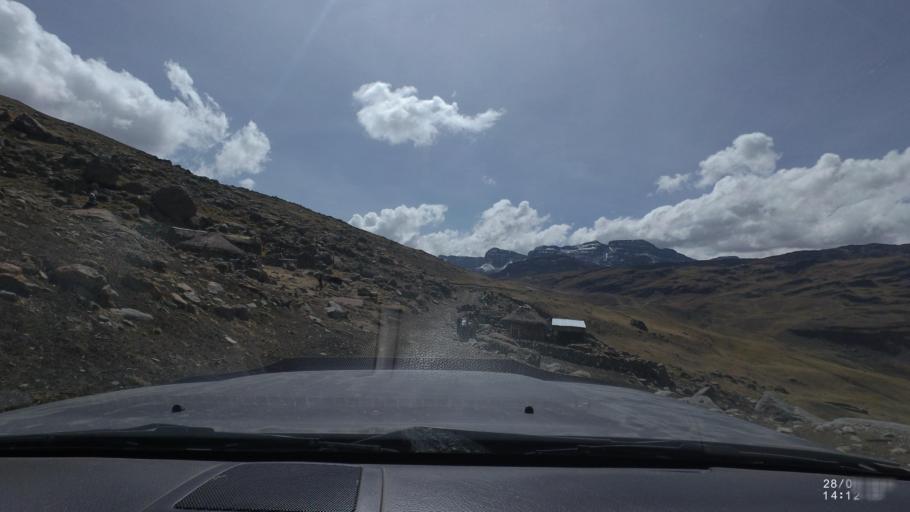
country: BO
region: Cochabamba
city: Sipe Sipe
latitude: -17.2600
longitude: -66.3856
